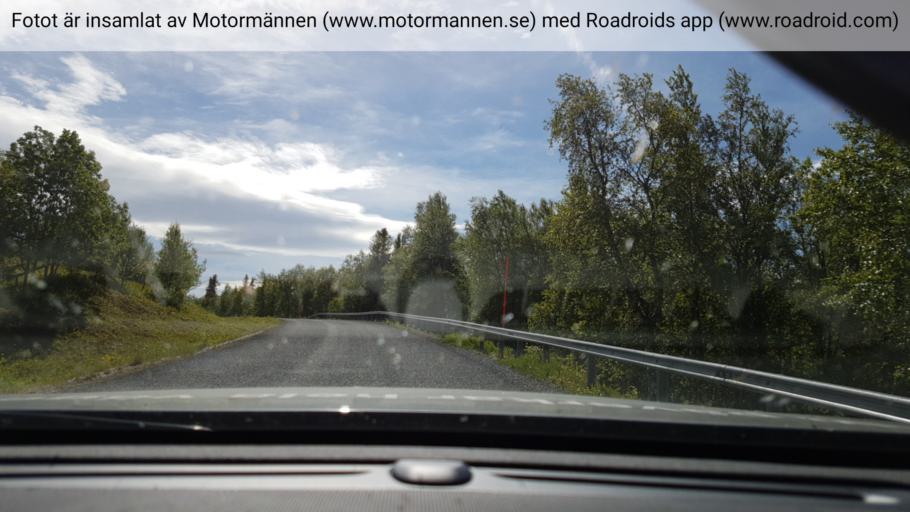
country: SE
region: Vaesterbotten
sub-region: Vilhelmina Kommun
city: Sjoberg
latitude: 65.2864
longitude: 15.2939
